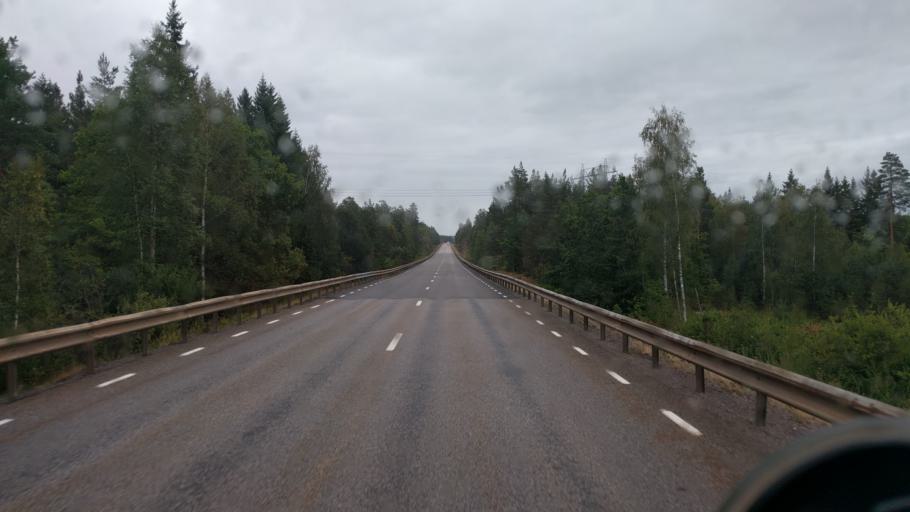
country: SE
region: Kalmar
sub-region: Vasterviks Kommun
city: Ankarsrum
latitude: 57.7005
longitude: 16.2484
